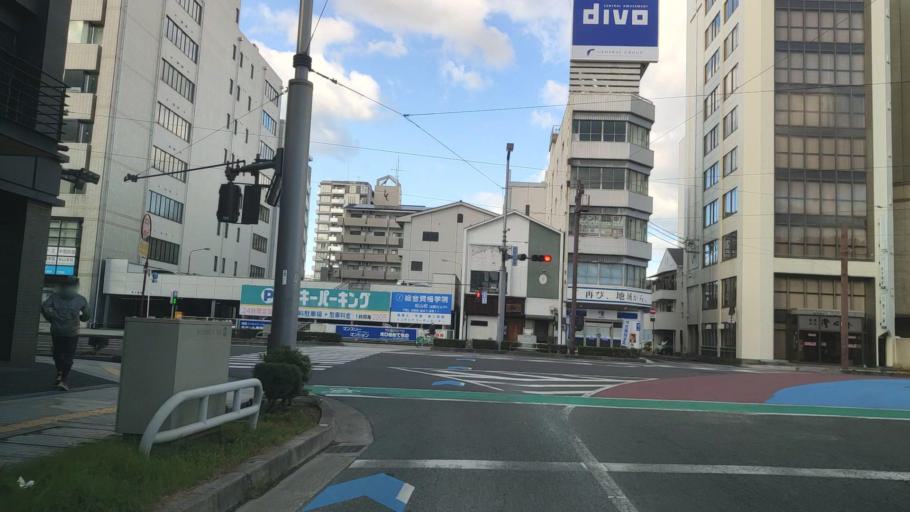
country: JP
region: Ehime
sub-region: Shikoku-chuo Shi
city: Matsuyama
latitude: 33.8393
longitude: 132.7591
